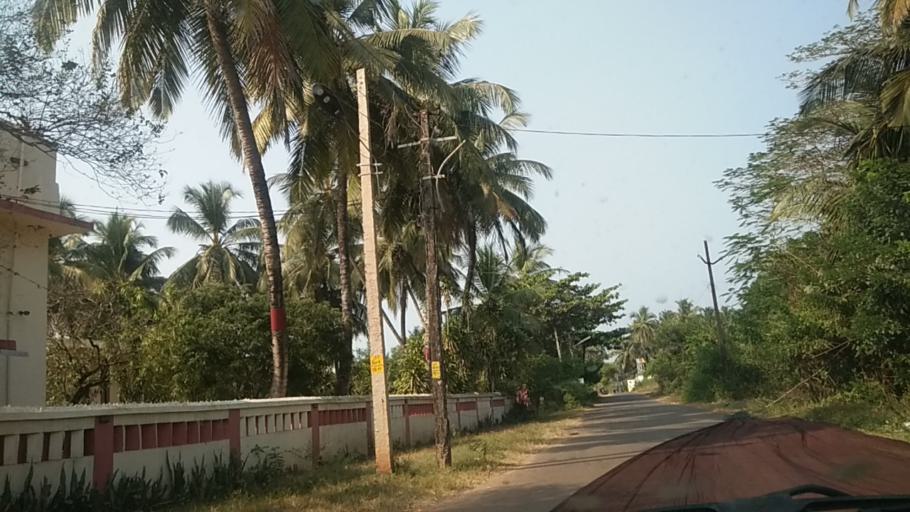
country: IN
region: Goa
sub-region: South Goa
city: Colva
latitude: 15.2866
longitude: 73.9121
